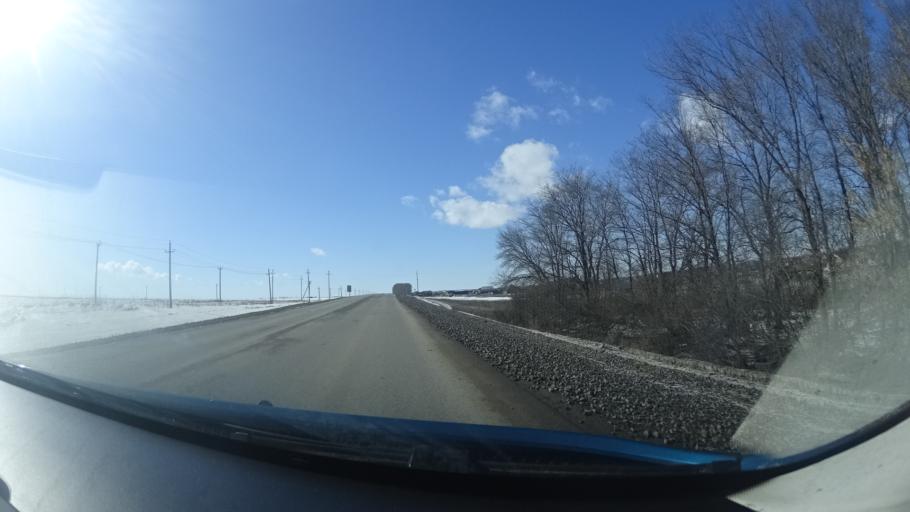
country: RU
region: Bashkortostan
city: Avdon
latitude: 54.6090
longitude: 55.8680
